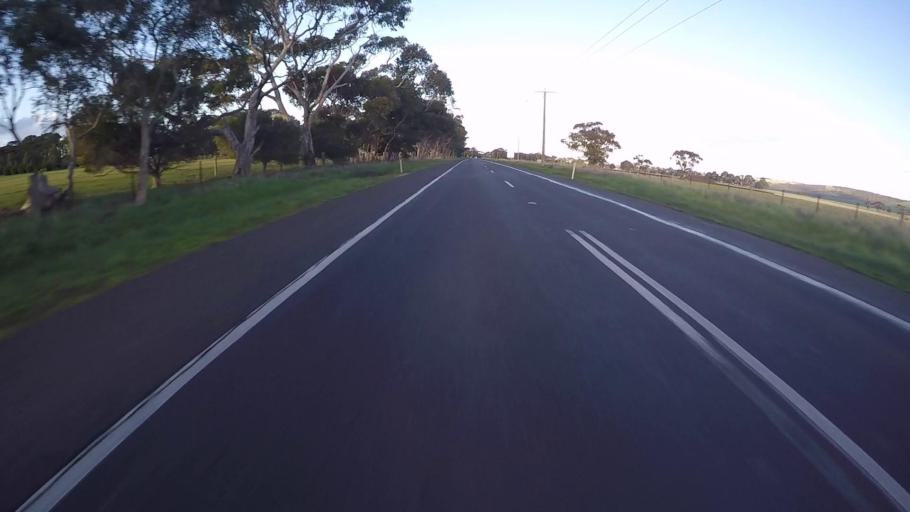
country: AU
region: Victoria
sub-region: Greater Geelong
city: Wandana Heights
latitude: -38.1225
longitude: 144.2192
